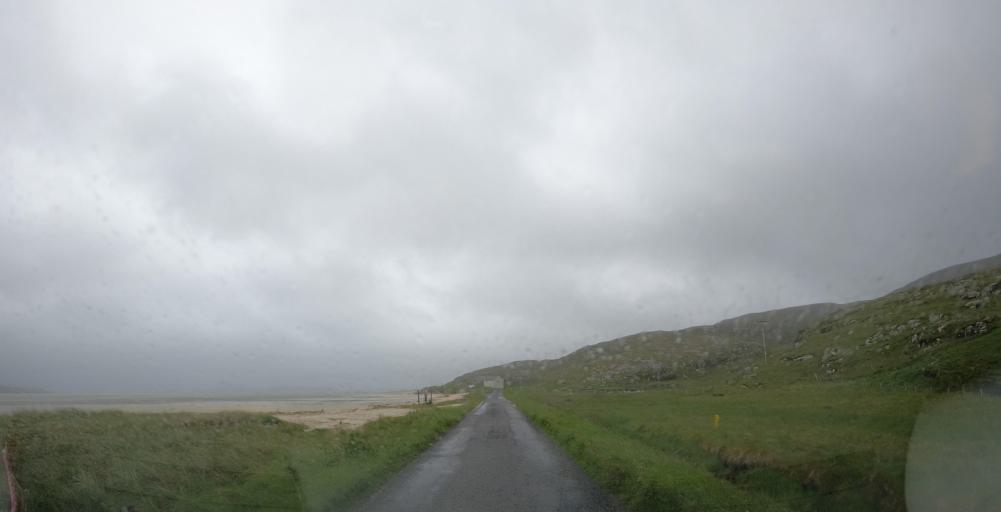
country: GB
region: Scotland
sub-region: Eilean Siar
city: Barra
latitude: 57.0200
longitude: -7.4465
